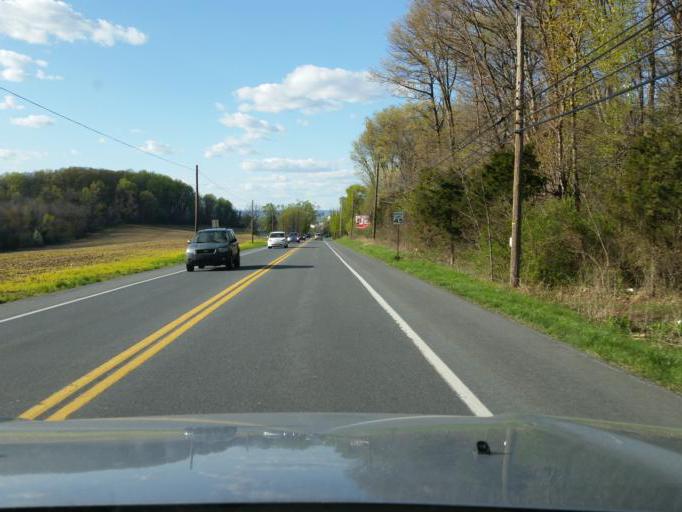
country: US
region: Pennsylvania
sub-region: Dauphin County
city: Hershey
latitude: 40.2426
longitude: -76.6256
